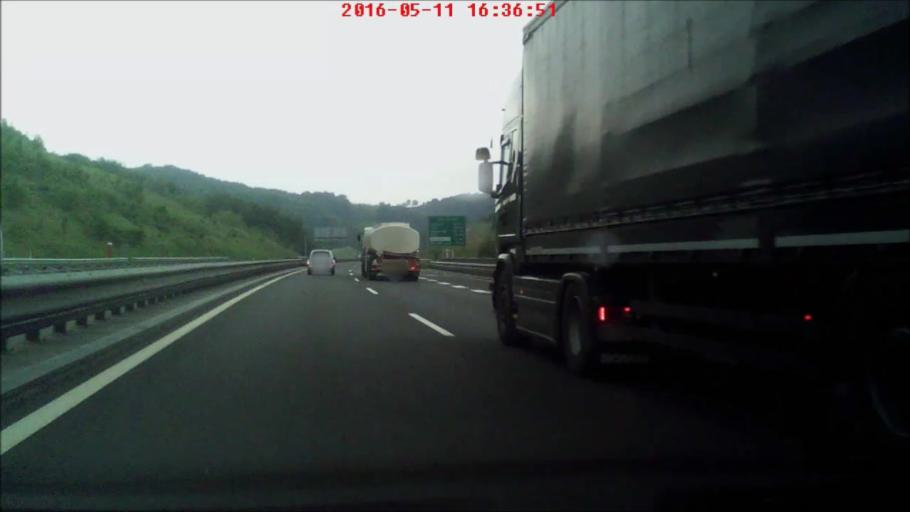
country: SI
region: Pesnica
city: Pesnica pri Mariboru
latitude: 46.5779
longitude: 15.6897
